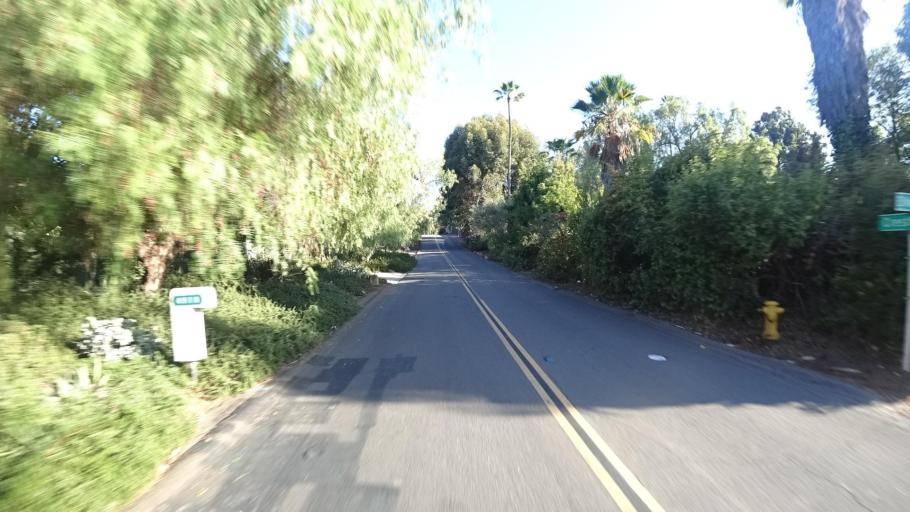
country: US
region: California
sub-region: San Diego County
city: Casa de Oro-Mount Helix
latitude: 32.7683
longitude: -116.9692
